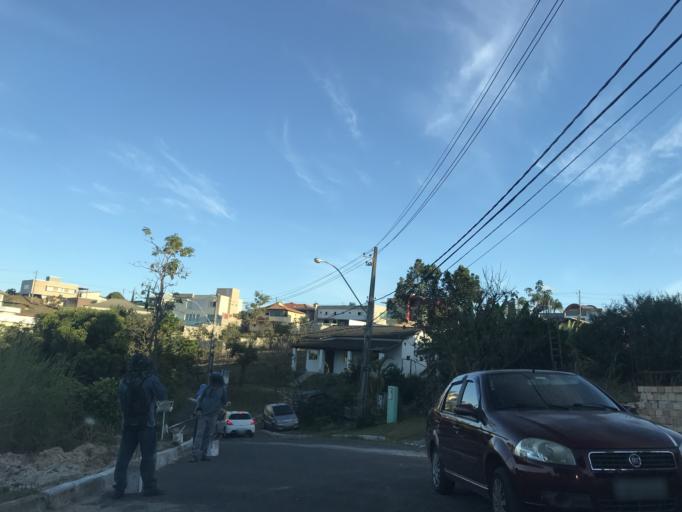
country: BR
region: Federal District
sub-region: Brasilia
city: Brasilia
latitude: -15.8826
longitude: -47.7646
